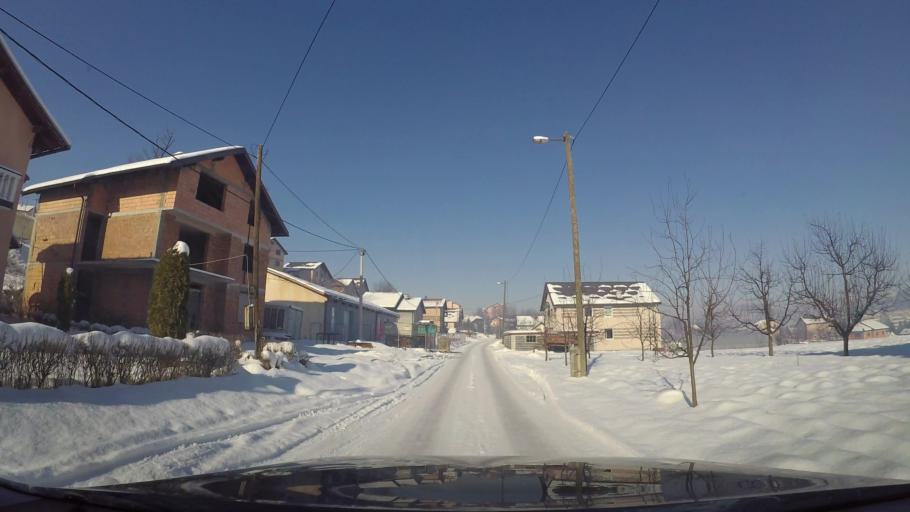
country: BA
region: Federation of Bosnia and Herzegovina
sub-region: Kanton Sarajevo
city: Sarajevo
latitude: 43.8189
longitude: 18.3735
